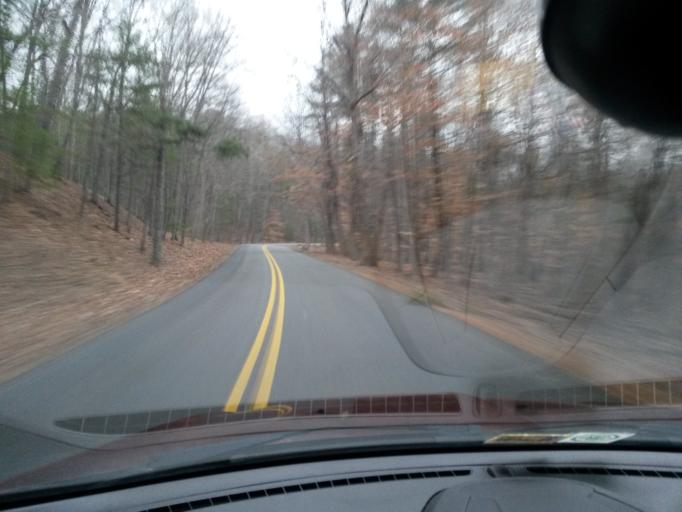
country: US
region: Virginia
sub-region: Alleghany County
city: Clifton Forge
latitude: 37.8785
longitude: -79.8095
